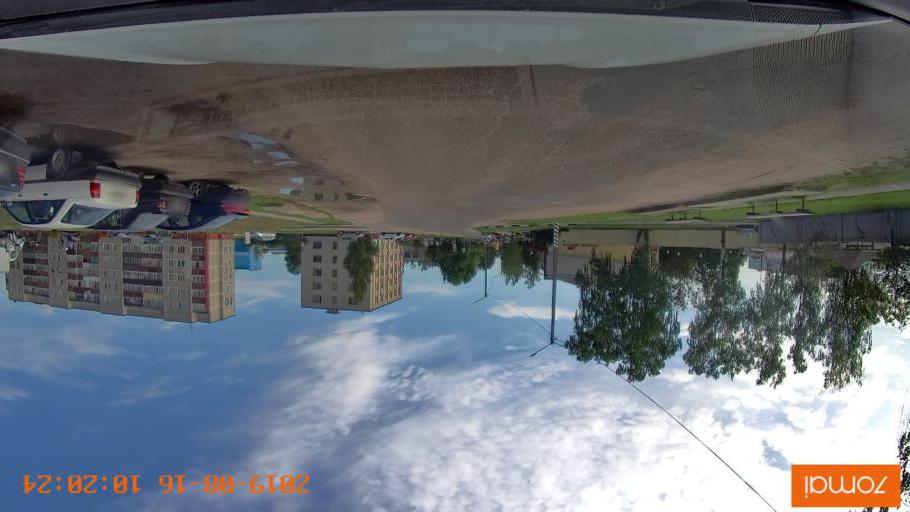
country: BY
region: Mogilev
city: Asipovichy
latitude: 53.3005
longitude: 28.6617
